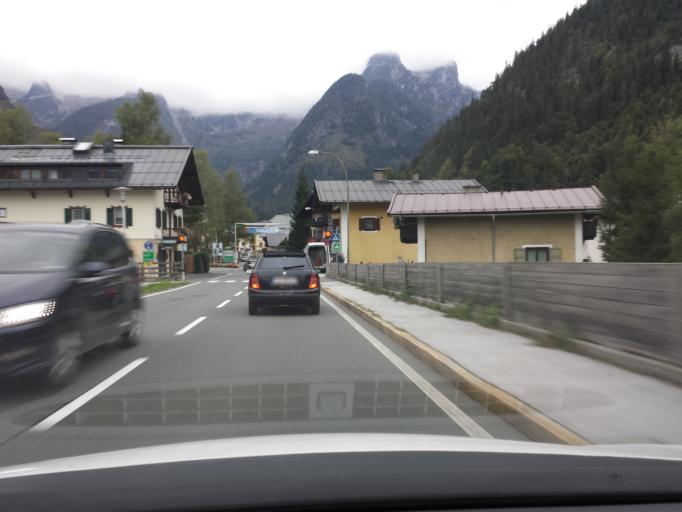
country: AT
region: Salzburg
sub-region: Politischer Bezirk Zell am See
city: Lofer
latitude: 47.5887
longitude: 12.6947
